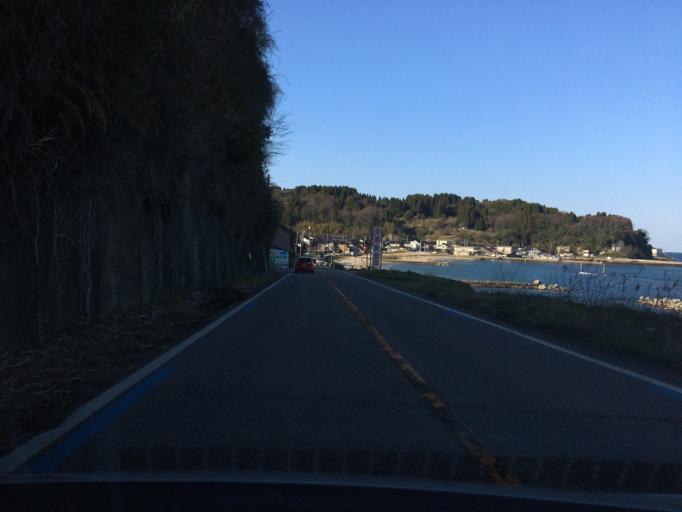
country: JP
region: Toyama
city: Himi
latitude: 36.9088
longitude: 137.0167
